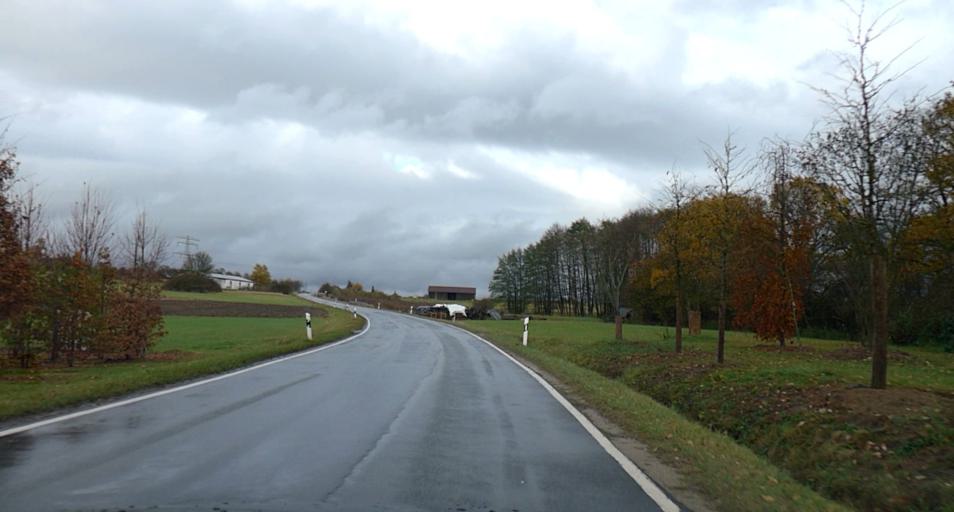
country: DE
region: Bavaria
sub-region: Upper Franconia
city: Effeltrich
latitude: 49.6666
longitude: 11.1168
